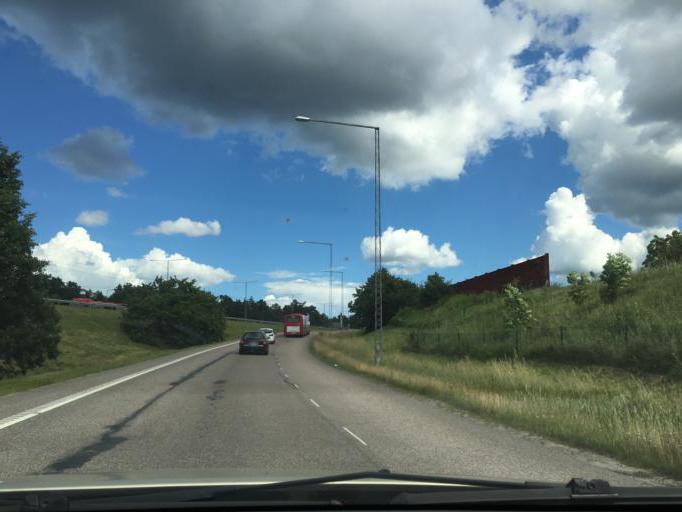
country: SE
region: Stockholm
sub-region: Nacka Kommun
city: Nacka
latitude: 59.3141
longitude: 18.1845
